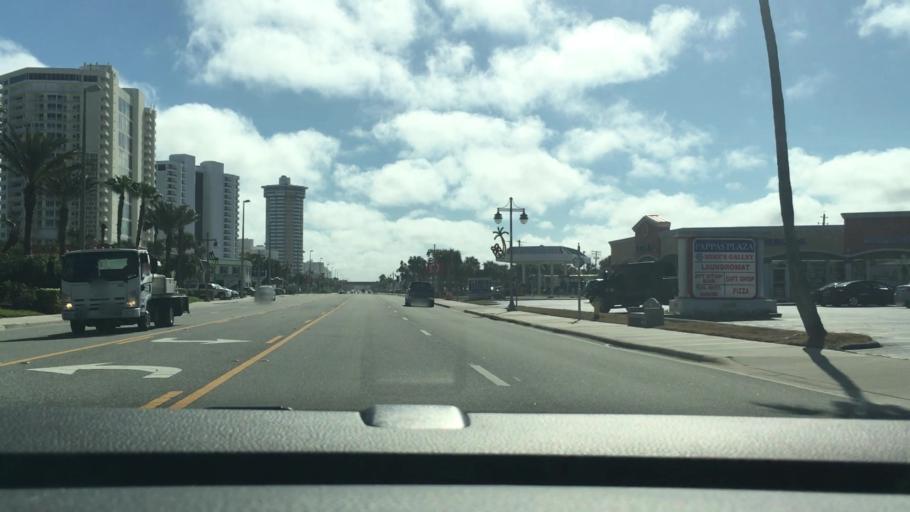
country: US
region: Florida
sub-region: Volusia County
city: Daytona Beach Shores
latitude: 29.1872
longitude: -80.9886
